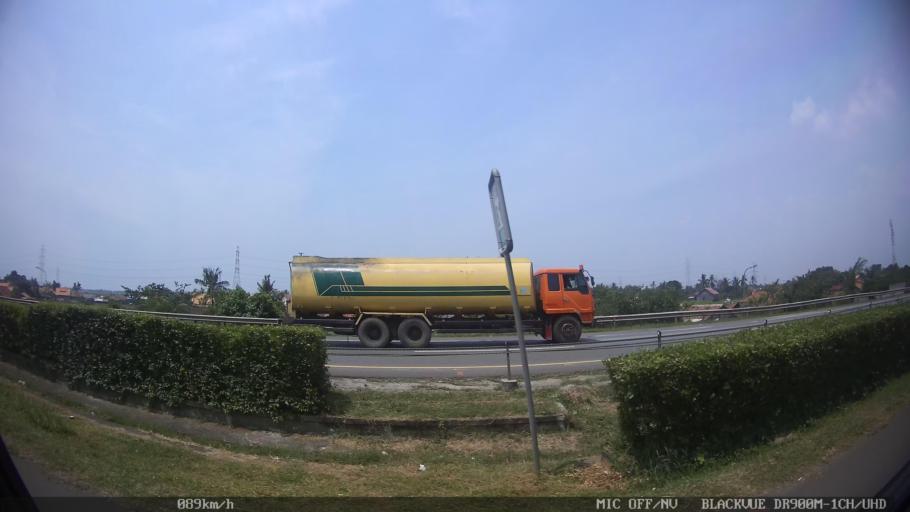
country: ID
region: Banten
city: Serang
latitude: -6.0587
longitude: 106.1218
